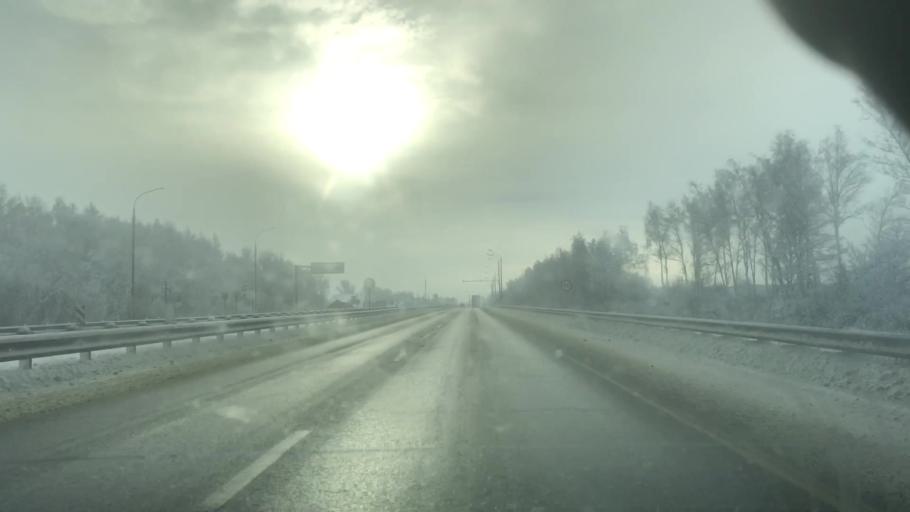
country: RU
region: Tula
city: Venev
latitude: 54.3480
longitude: 38.1546
